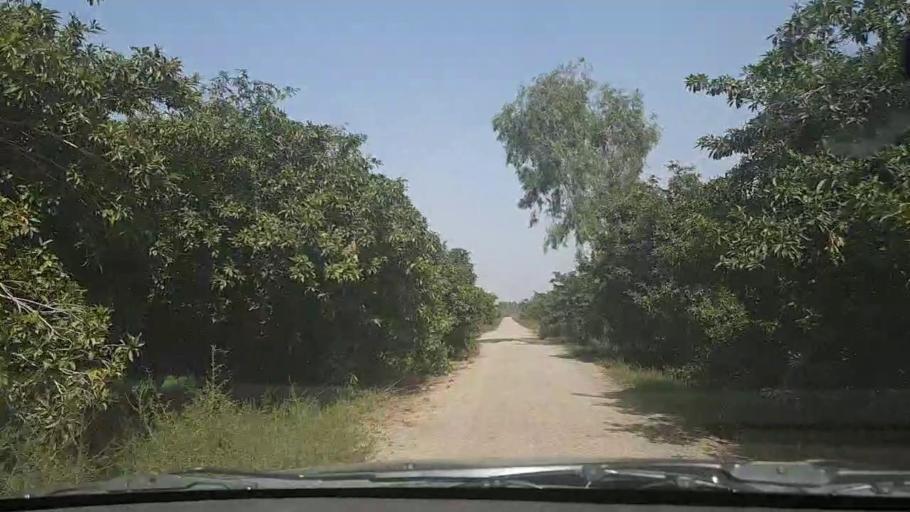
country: PK
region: Sindh
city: Keti Bandar
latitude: 24.1987
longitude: 67.5455
